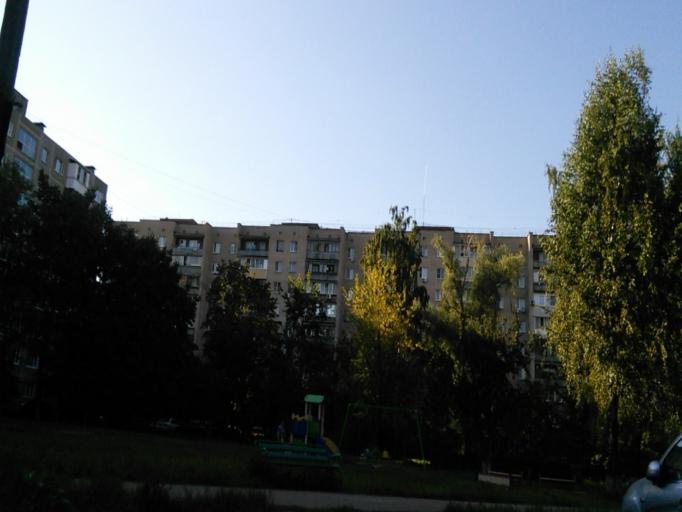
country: RU
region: Moskovskaya
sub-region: Podol'skiy Rayon
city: Podol'sk
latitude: 55.4409
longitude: 37.5654
